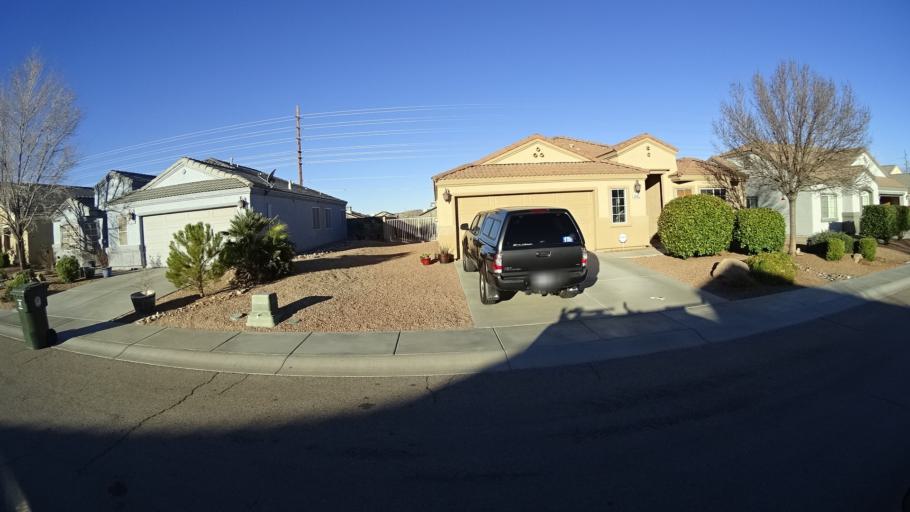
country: US
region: Arizona
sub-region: Mohave County
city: New Kingman-Butler
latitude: 35.2234
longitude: -113.9931
